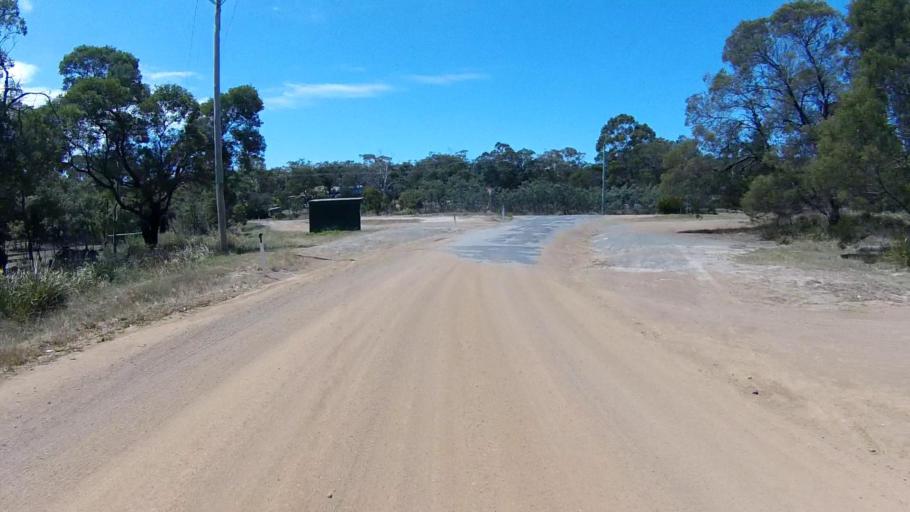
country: AU
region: Tasmania
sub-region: Clarence
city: Sandford
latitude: -42.9638
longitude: 147.4733
